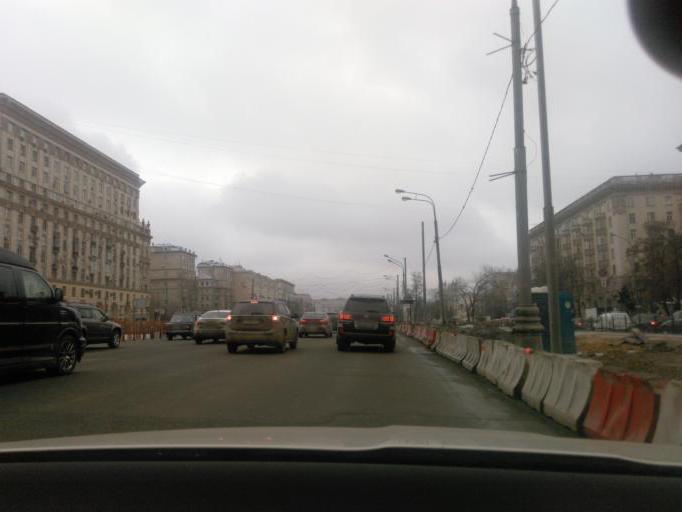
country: RU
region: Moskovskaya
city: Dorogomilovo
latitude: 55.7816
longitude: 37.5739
